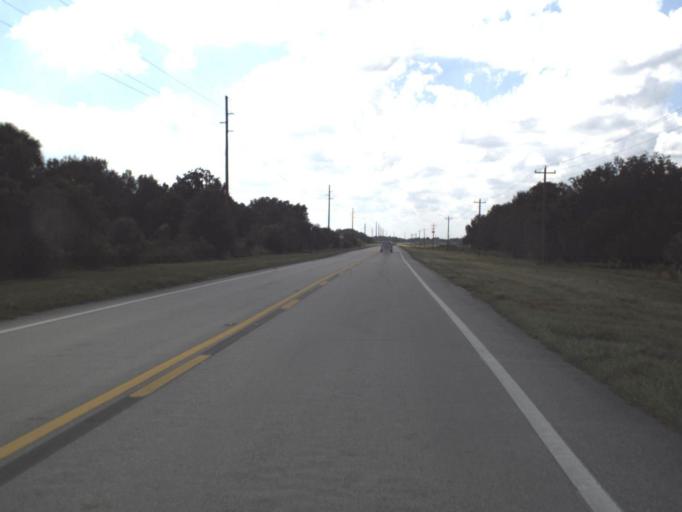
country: US
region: Florida
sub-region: Okeechobee County
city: Okeechobee
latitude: 27.3860
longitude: -81.0386
